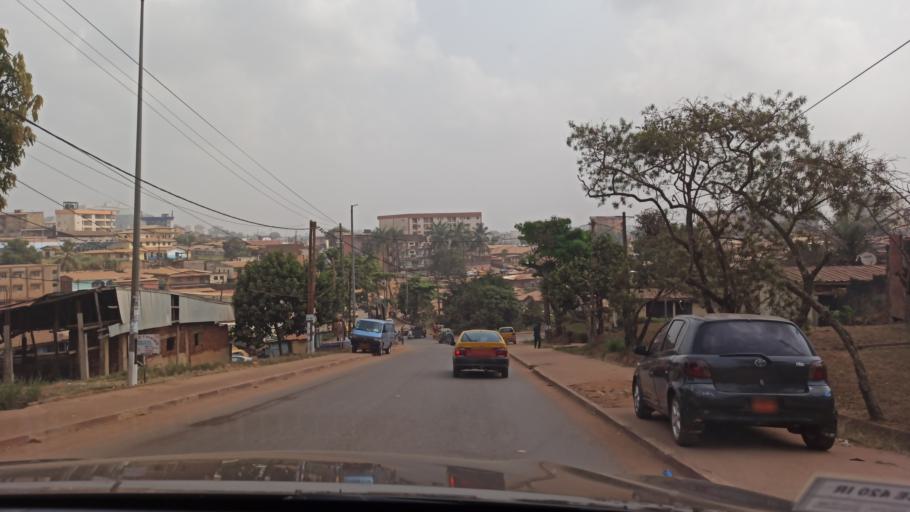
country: CM
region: Centre
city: Yaounde
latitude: 3.8786
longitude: 11.4906
